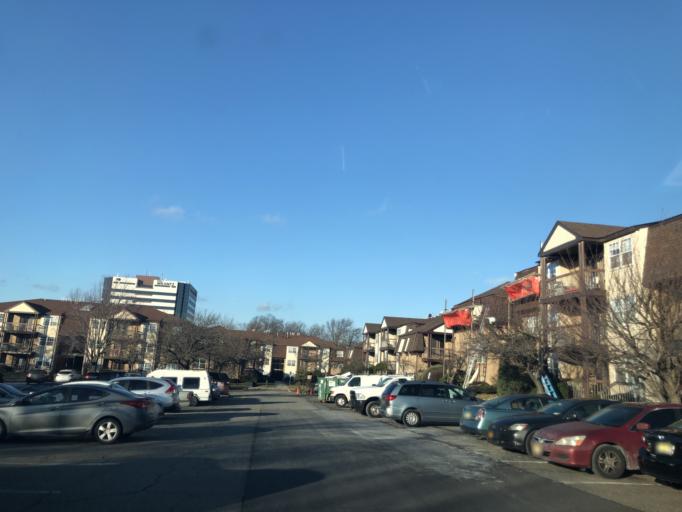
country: US
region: New Jersey
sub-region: Middlesex County
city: Woodbridge
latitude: 40.5485
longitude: -74.2988
